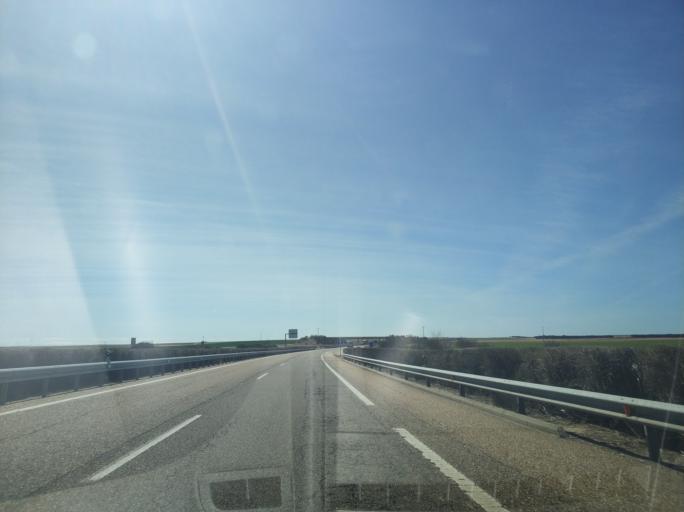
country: ES
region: Castille and Leon
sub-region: Provincia de Valladolid
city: Alaejos
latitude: 41.3010
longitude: -5.2304
